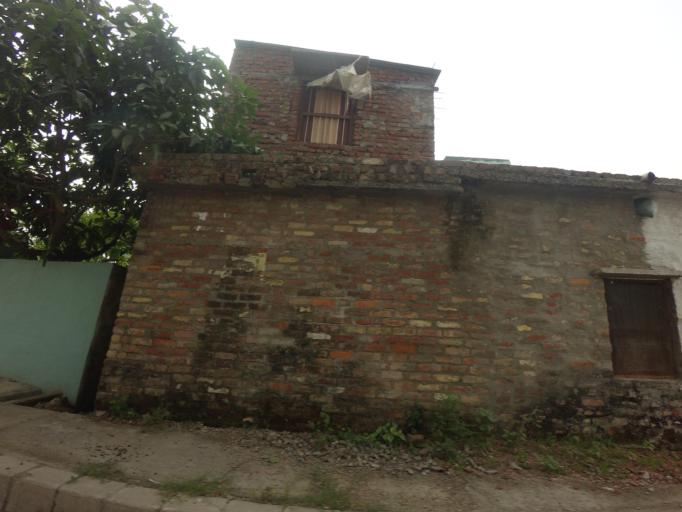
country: NP
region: Western Region
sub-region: Lumbini Zone
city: Bhairahawa
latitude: 27.4925
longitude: 83.4477
